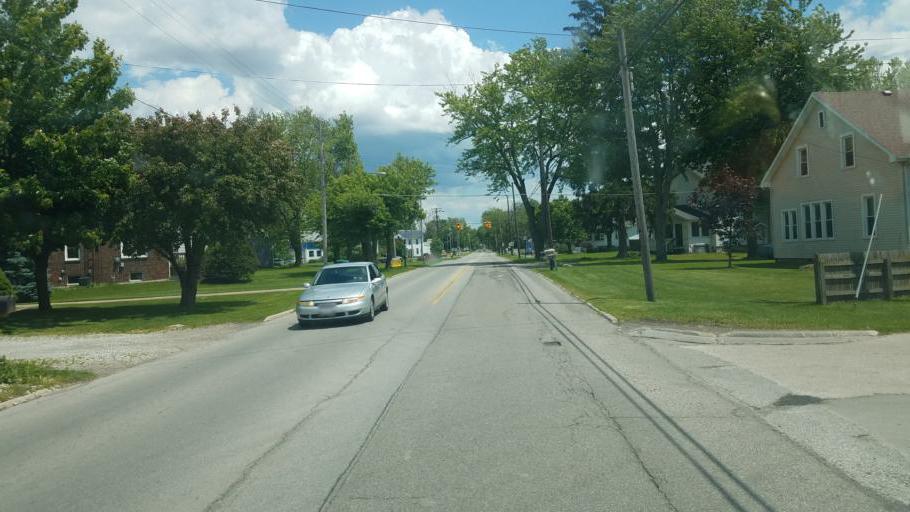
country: US
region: Ohio
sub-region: Crawford County
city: Crestline
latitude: 40.7919
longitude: -82.7487
